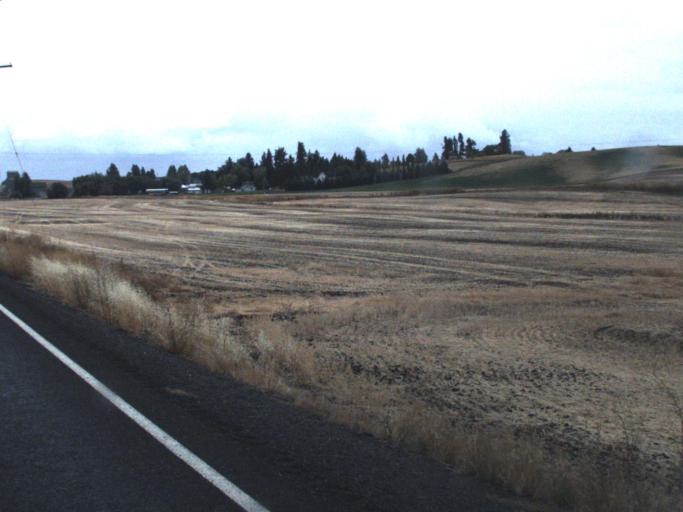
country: US
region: Washington
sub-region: Whitman County
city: Colfax
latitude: 47.1392
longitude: -117.2471
